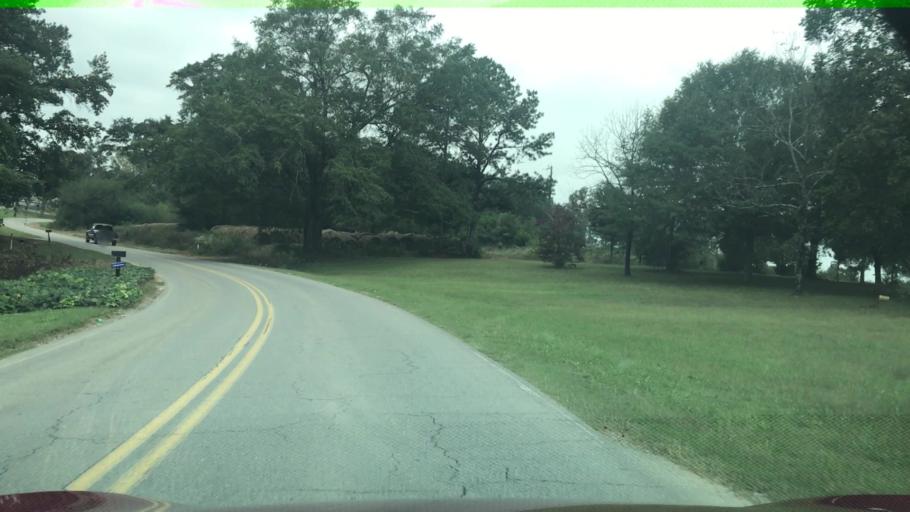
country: US
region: Alabama
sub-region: Cullman County
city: Good Hope
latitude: 34.0971
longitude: -87.0492
